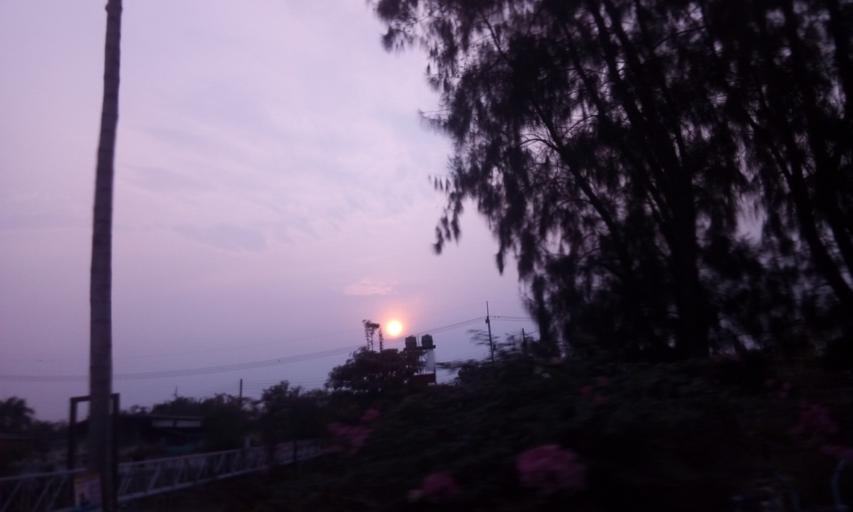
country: TH
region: Bangkok
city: Nong Chok
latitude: 13.9599
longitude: 100.8954
